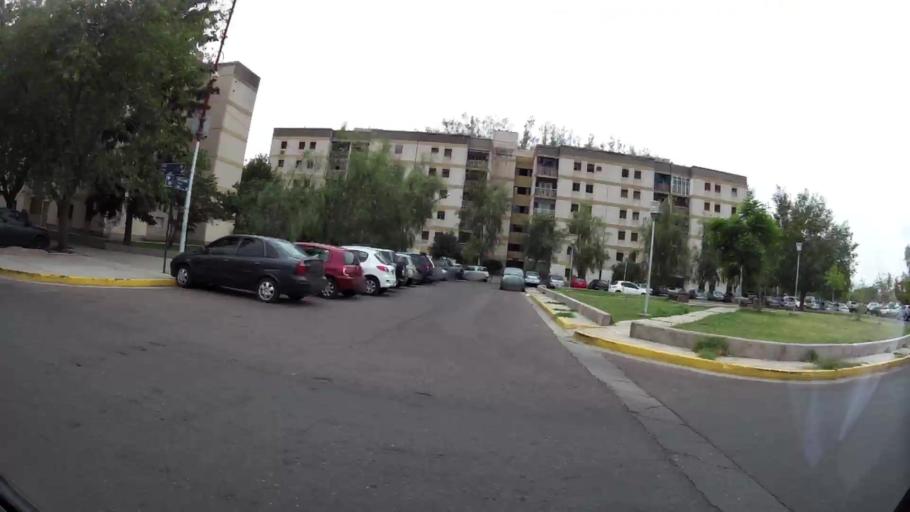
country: AR
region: Mendoza
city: Mendoza
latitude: -32.8741
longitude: -68.8418
